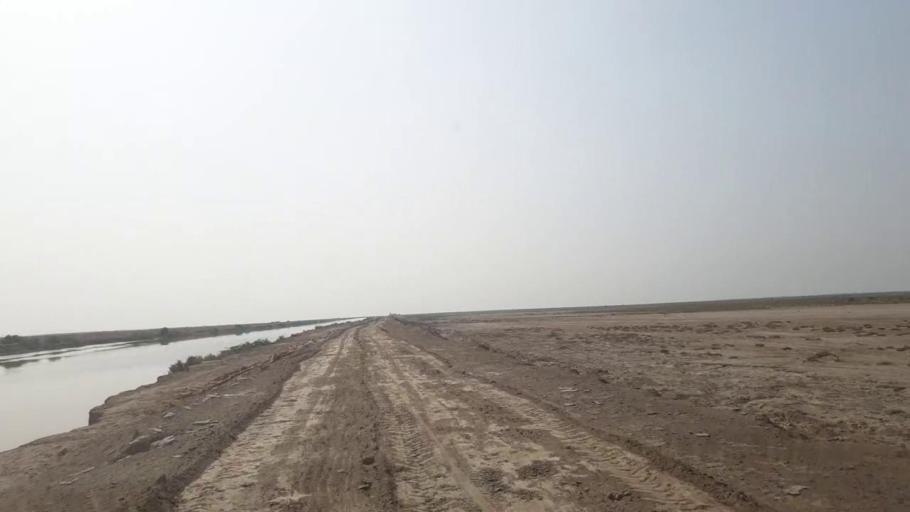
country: PK
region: Sindh
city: Kadhan
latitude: 24.3349
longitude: 68.8413
